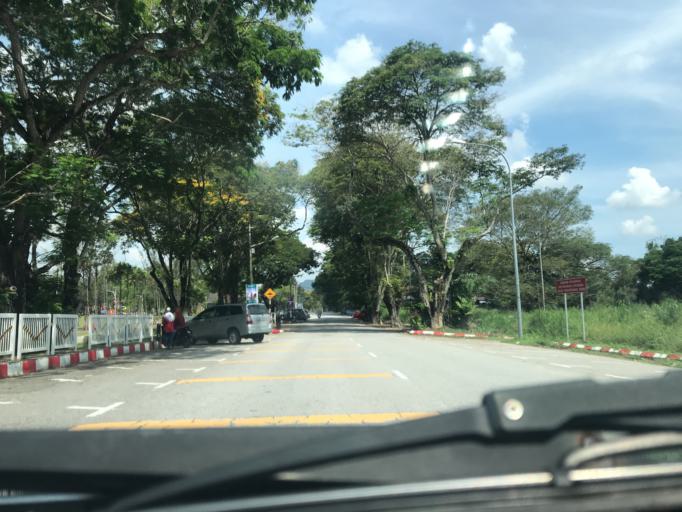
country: MY
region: Perak
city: Ipoh
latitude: 4.5975
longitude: 101.1088
